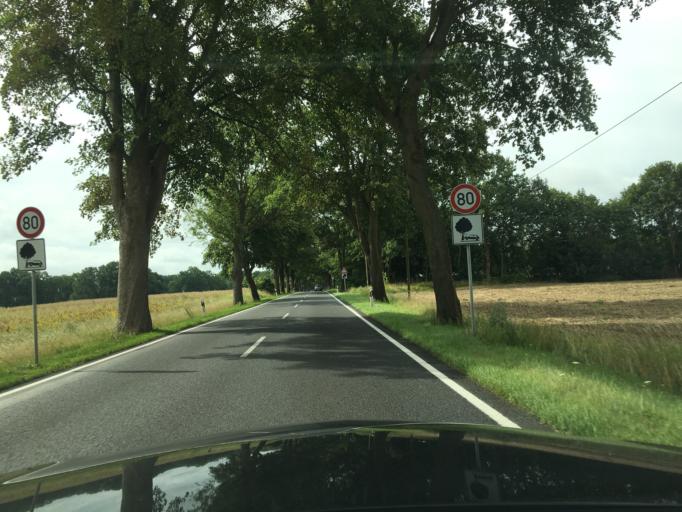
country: DE
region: Brandenburg
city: Gransee
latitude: 52.9166
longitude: 13.1577
